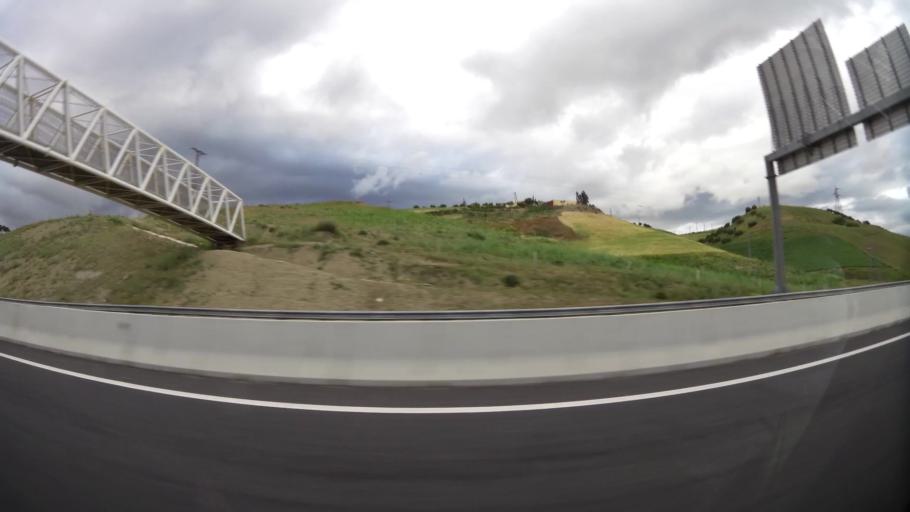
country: MA
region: Taza-Al Hoceima-Taounate
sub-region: Taza
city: Taza
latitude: 34.2607
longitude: -3.9477
